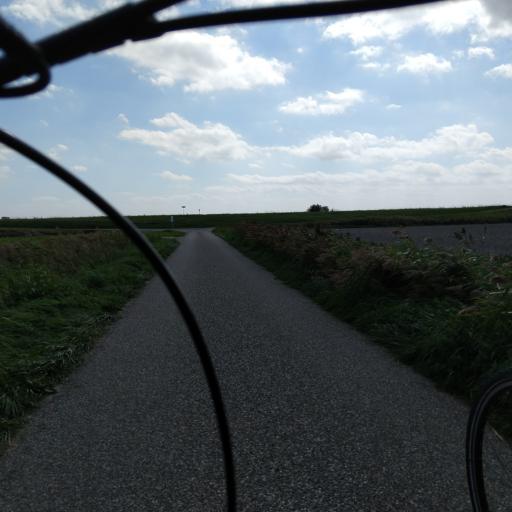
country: NL
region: Zeeland
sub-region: Gemeente Noord-Beveland
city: Kamperland
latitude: 51.5910
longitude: 3.7634
